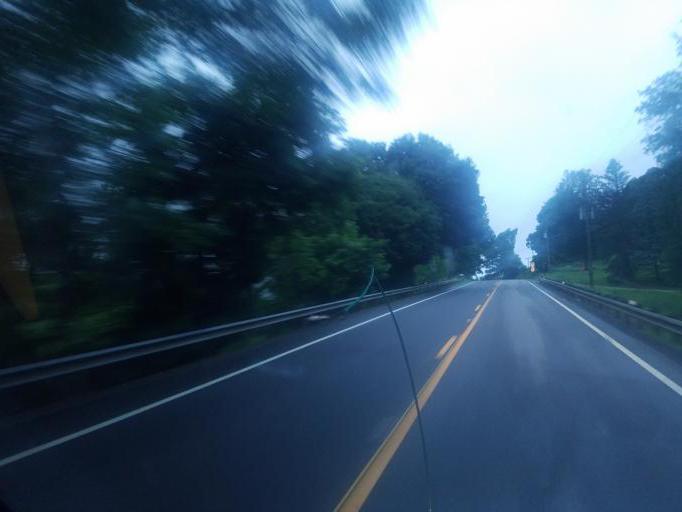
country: US
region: Ohio
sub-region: Carroll County
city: Carrollton
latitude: 40.5447
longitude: -81.0357
